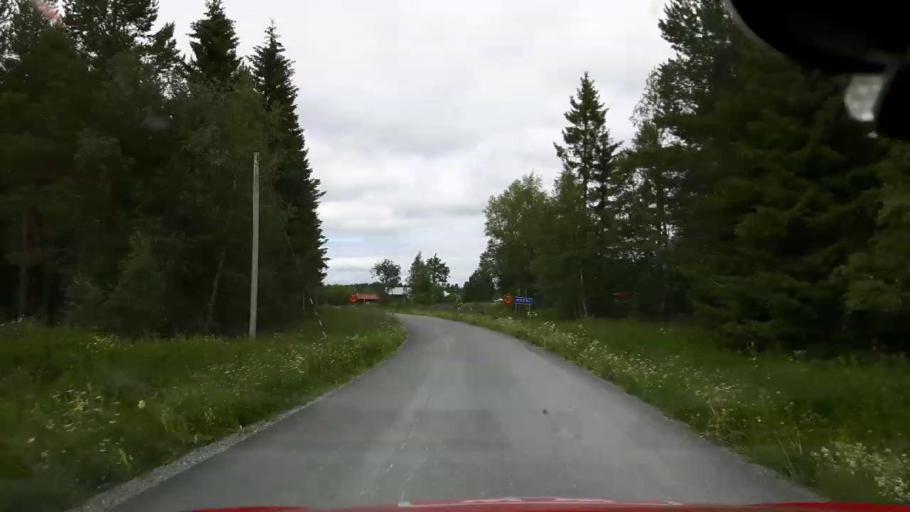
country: SE
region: Jaemtland
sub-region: OEstersunds Kommun
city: Brunflo
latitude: 63.0688
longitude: 14.8942
